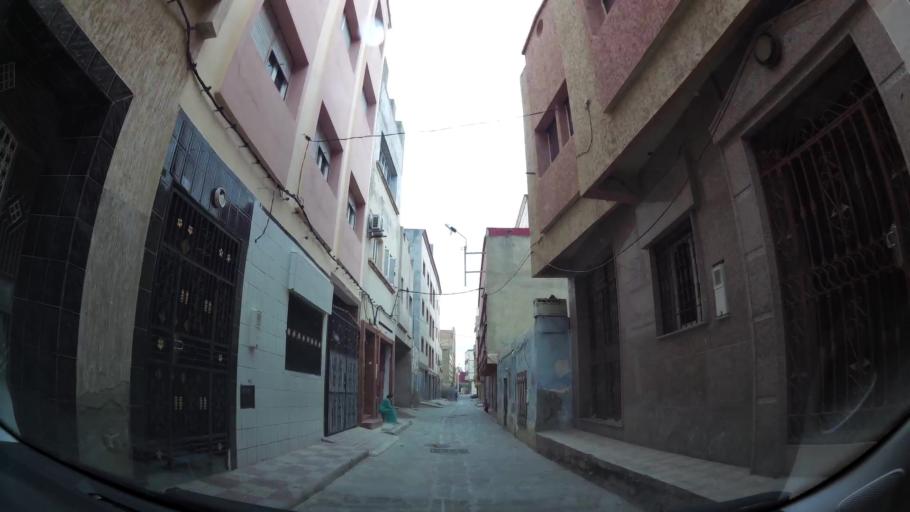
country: MA
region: Oriental
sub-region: Nador
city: Nador
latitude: 35.1623
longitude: -2.9317
